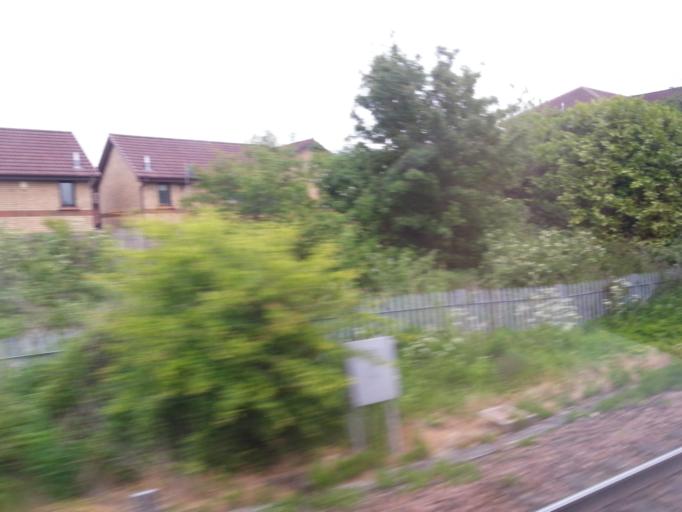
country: GB
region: Scotland
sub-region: Perth and Kinross
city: Perth
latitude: 56.4079
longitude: -3.4522
